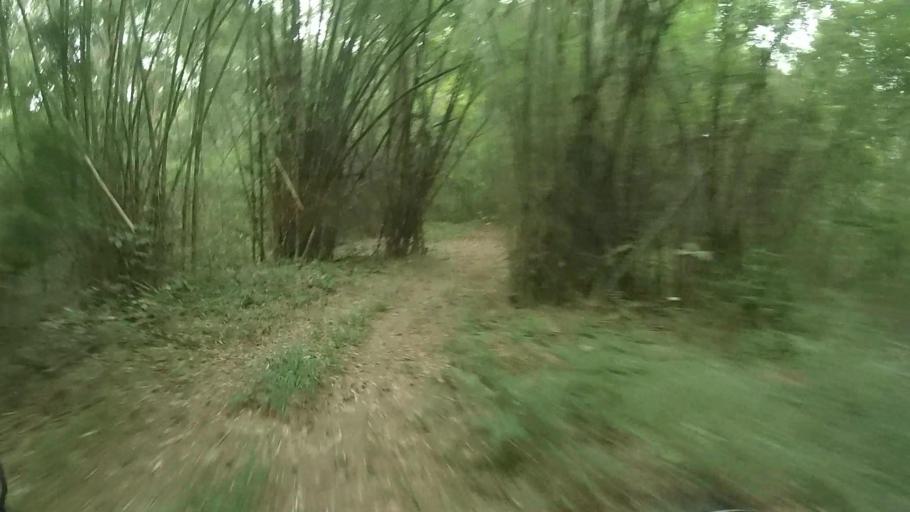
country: TH
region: Chiang Mai
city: Mae On
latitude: 18.8842
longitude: 99.2062
